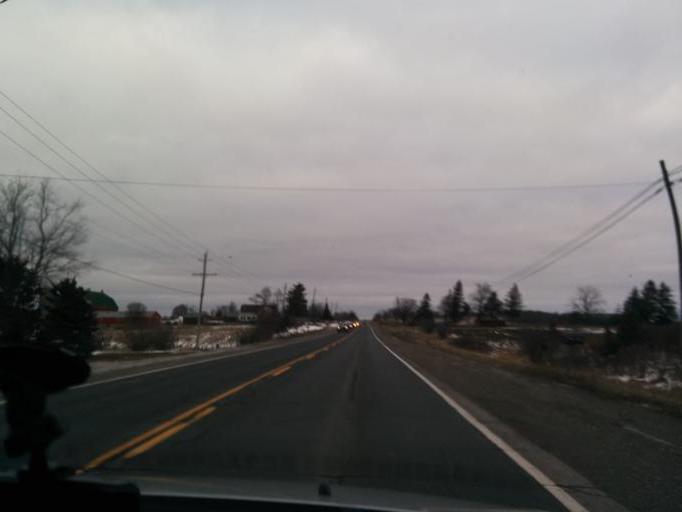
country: CA
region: Ontario
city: Ancaster
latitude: 43.0271
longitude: -79.9932
